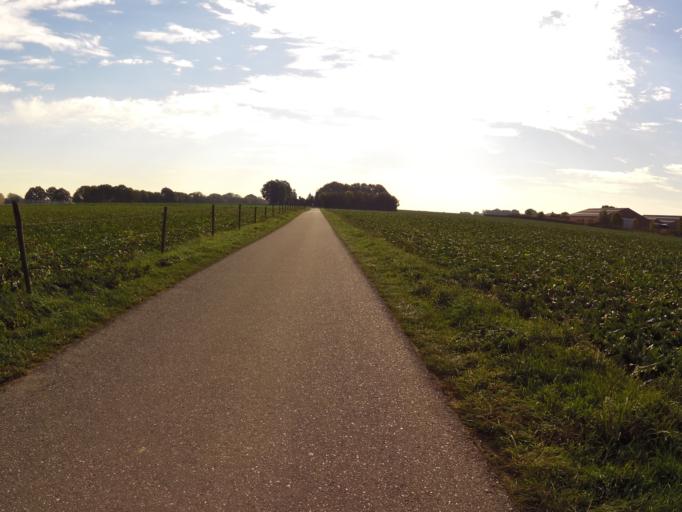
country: NL
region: Limburg
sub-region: Gemeente Schinnen
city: Doenrade
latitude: 50.9627
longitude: 5.8914
